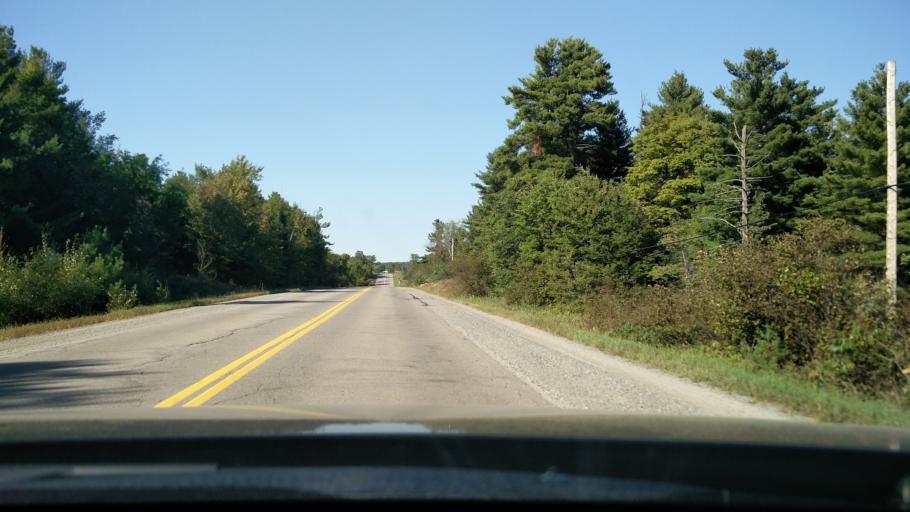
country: CA
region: Ontario
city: Perth
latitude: 44.7199
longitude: -76.4007
